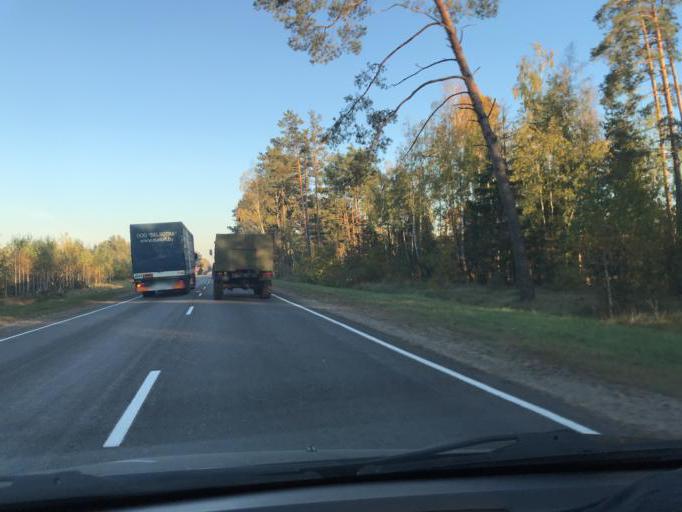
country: BY
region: Minsk
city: Staryya Darohi
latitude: 53.0483
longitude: 28.0821
